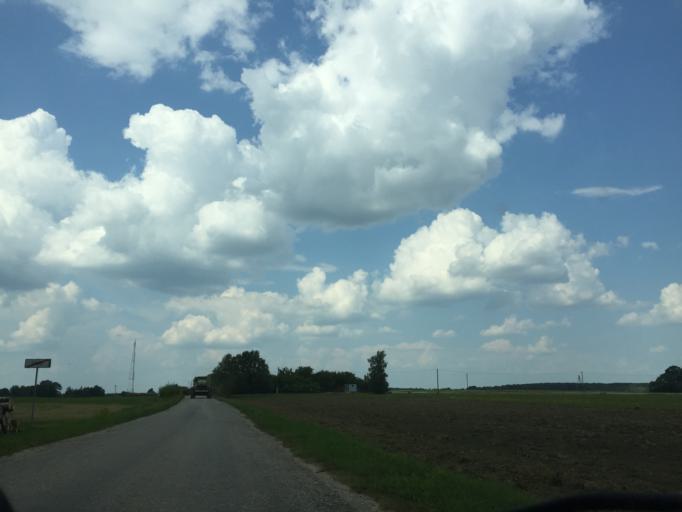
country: LT
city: Naujoji Akmene
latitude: 56.3466
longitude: 23.0603
